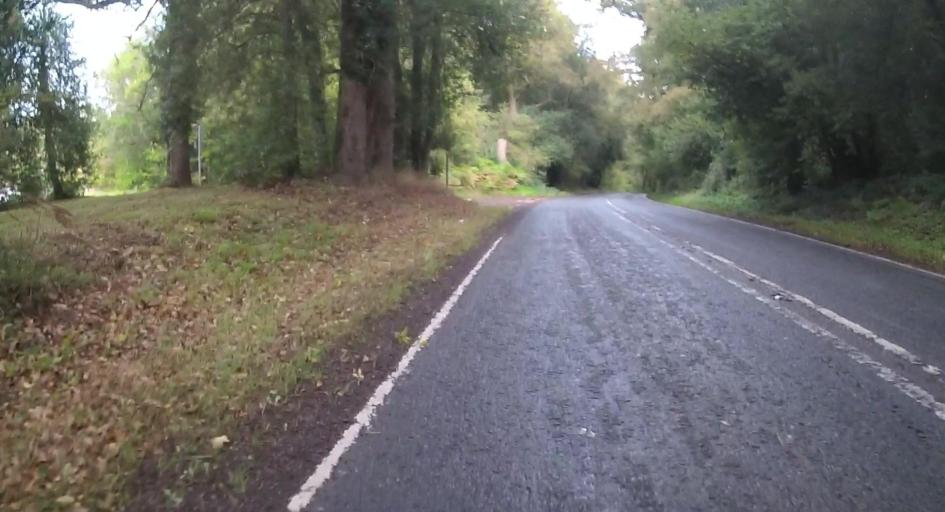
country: GB
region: England
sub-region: Hampshire
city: Odiham
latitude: 51.2730
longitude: -0.9261
